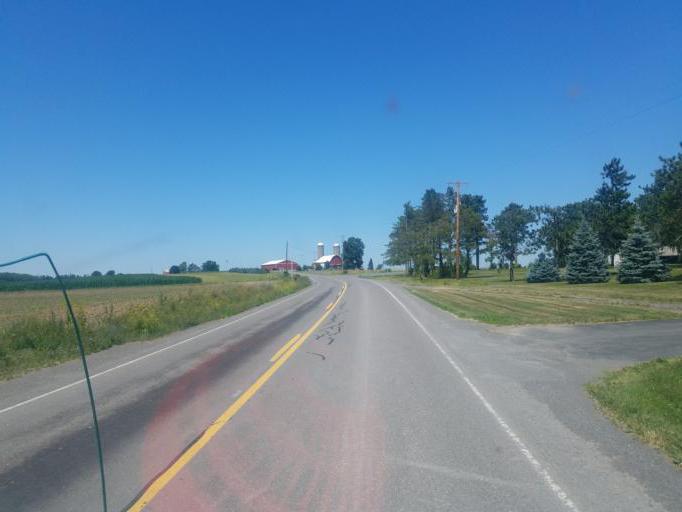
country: US
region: New York
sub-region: Yates County
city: Penn Yan
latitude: 42.6951
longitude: -76.9986
